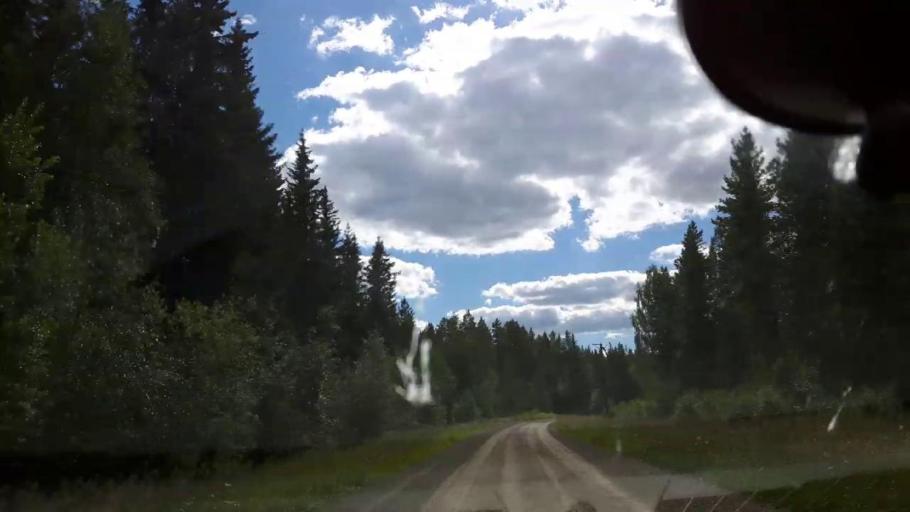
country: SE
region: Vaesternorrland
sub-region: Ange Kommun
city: Ange
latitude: 62.7667
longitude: 15.7339
